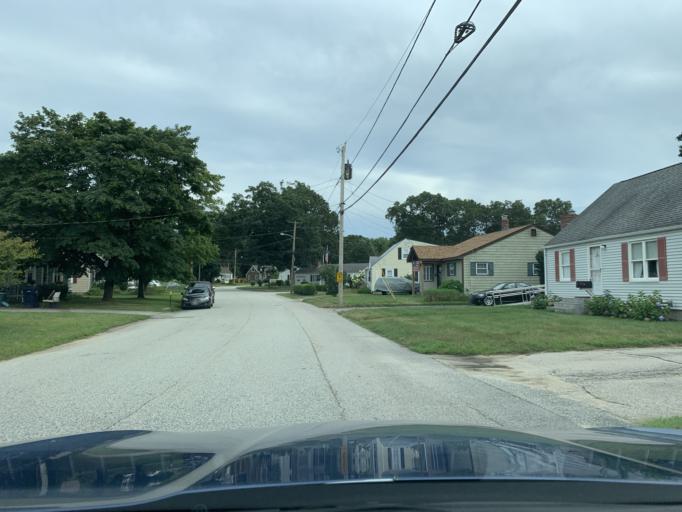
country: US
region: Rhode Island
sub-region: Kent County
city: East Greenwich
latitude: 41.6183
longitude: -71.4664
